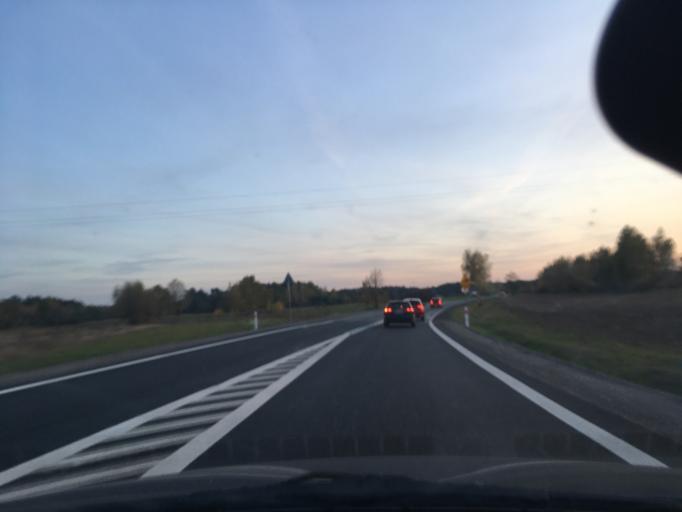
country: PL
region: Masovian Voivodeship
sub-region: Powiat plocki
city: Wyszogrod
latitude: 52.3554
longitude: 20.2091
